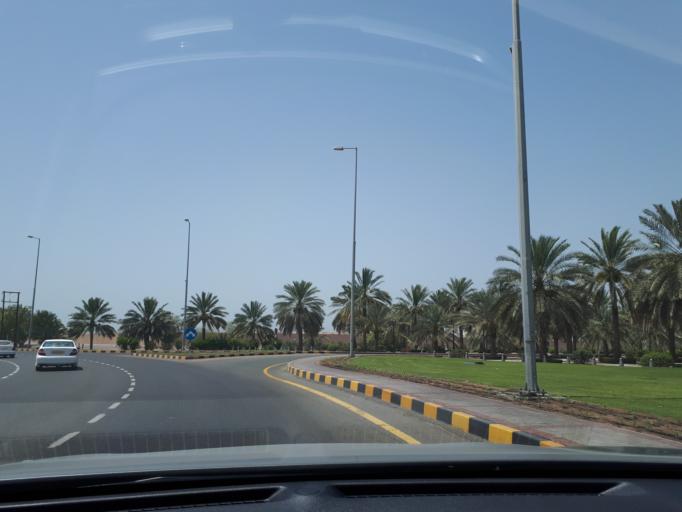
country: OM
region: Muhafazat Masqat
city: As Sib al Jadidah
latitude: 23.6904
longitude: 58.0817
